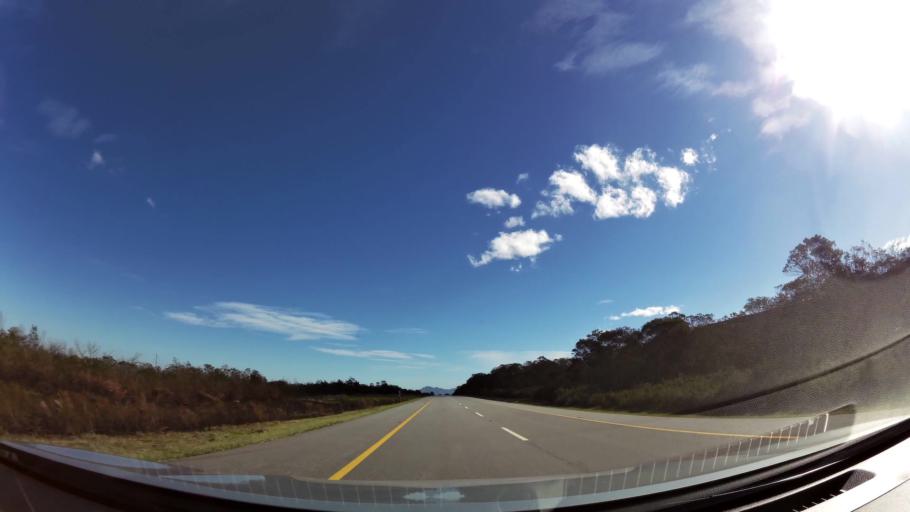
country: ZA
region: Eastern Cape
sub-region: Cacadu District Municipality
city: Kruisfontein
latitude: -33.9952
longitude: 24.7171
